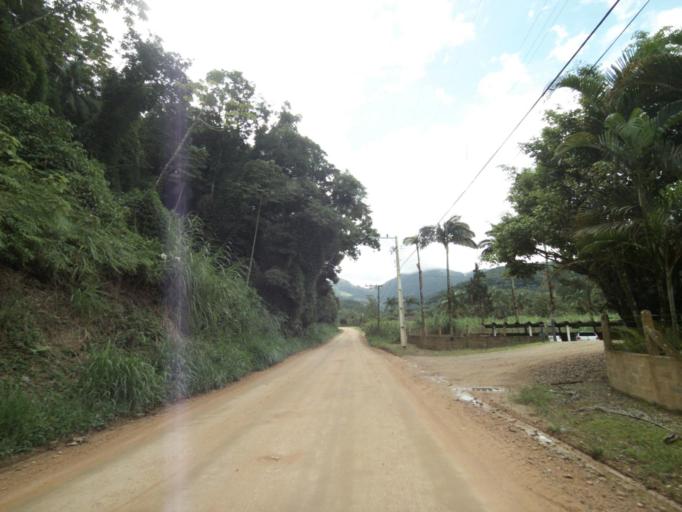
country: BR
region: Santa Catarina
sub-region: Pomerode
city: Pomerode
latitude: -26.7137
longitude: -49.2084
